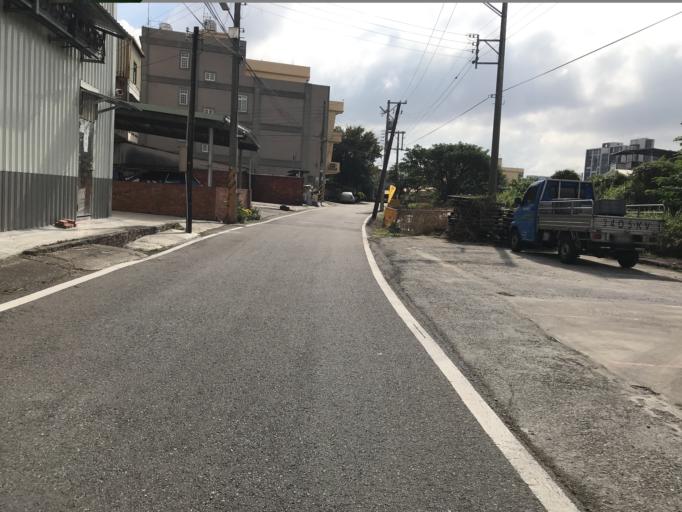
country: TW
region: Taiwan
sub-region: Hsinchu
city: Zhubei
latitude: 24.8137
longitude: 120.9966
